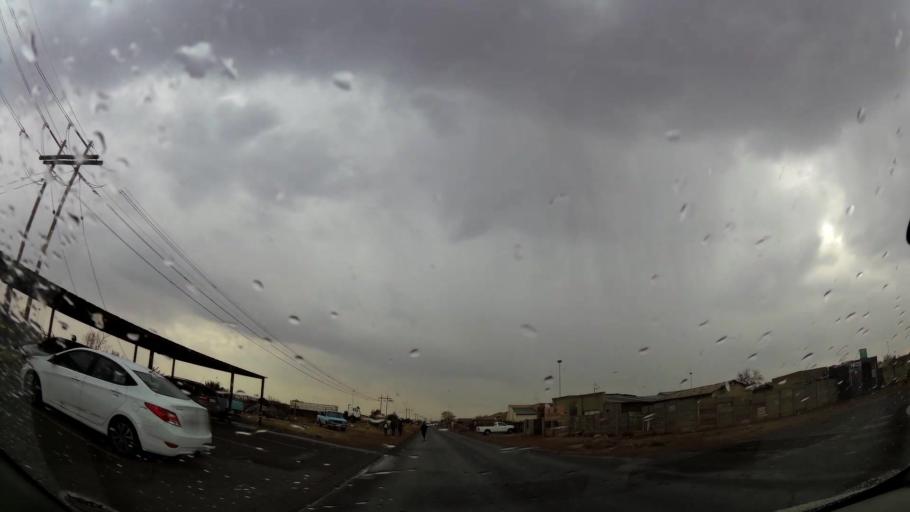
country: ZA
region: Gauteng
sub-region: Ekurhuleni Metropolitan Municipality
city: Germiston
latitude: -26.3588
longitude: 28.1612
